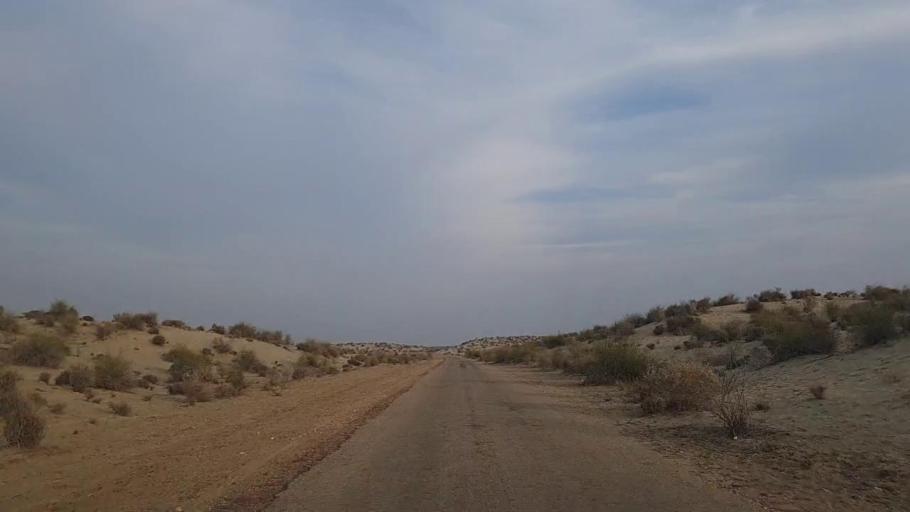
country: PK
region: Sindh
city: Jam Sahib
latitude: 26.4922
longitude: 68.5477
